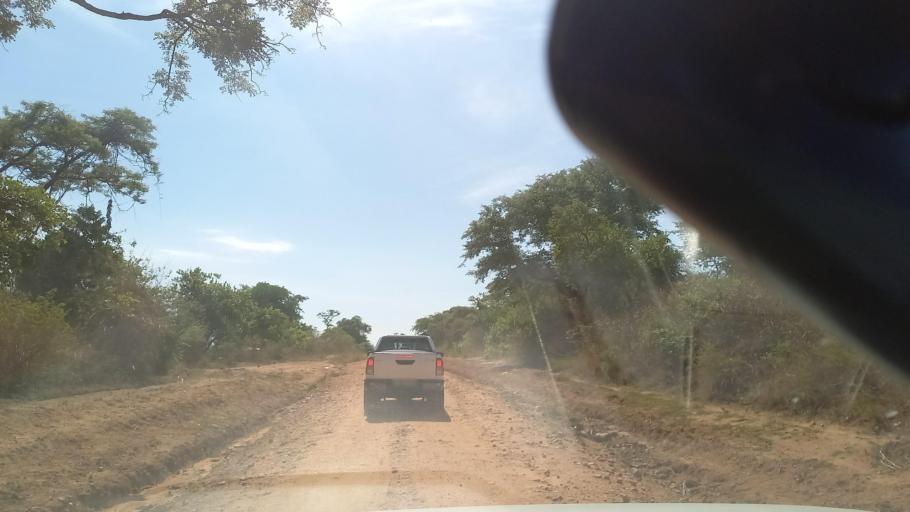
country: ZM
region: Southern
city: Mazabuka
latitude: -16.0408
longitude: 27.6211
